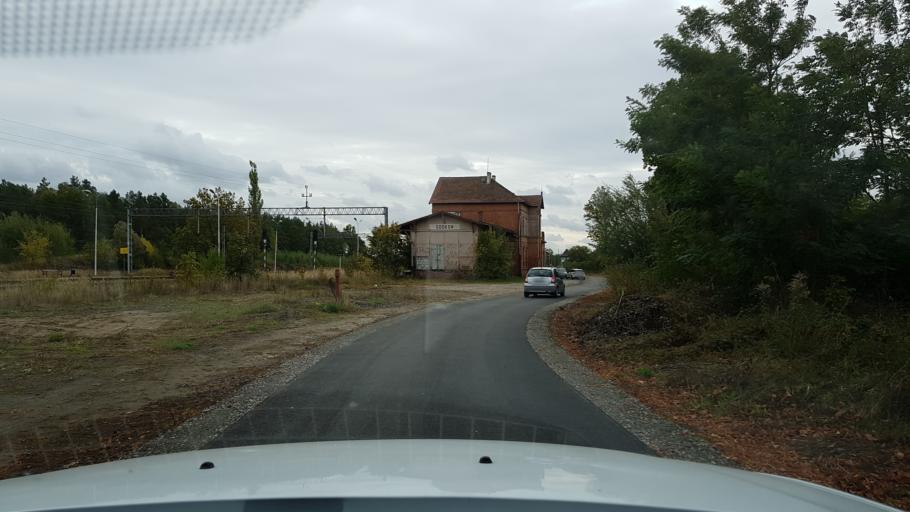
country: PL
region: West Pomeranian Voivodeship
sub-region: Powiat gryfinski
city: Chojna
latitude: 52.9013
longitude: 14.4580
